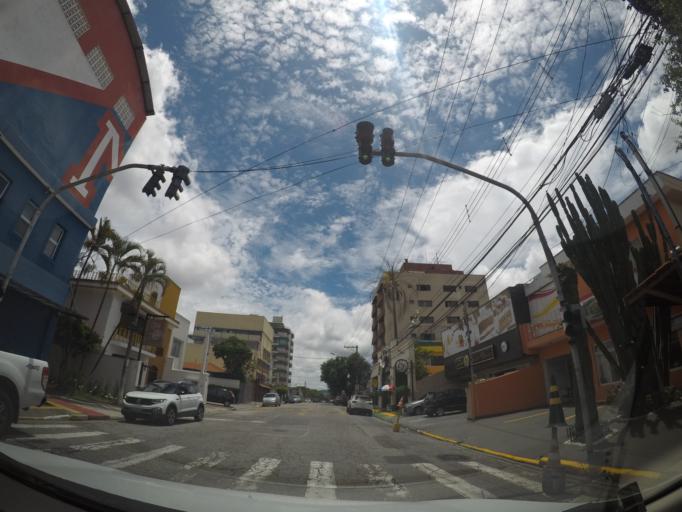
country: BR
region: Sao Paulo
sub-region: Guarulhos
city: Guarulhos
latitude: -23.4601
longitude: -46.5253
